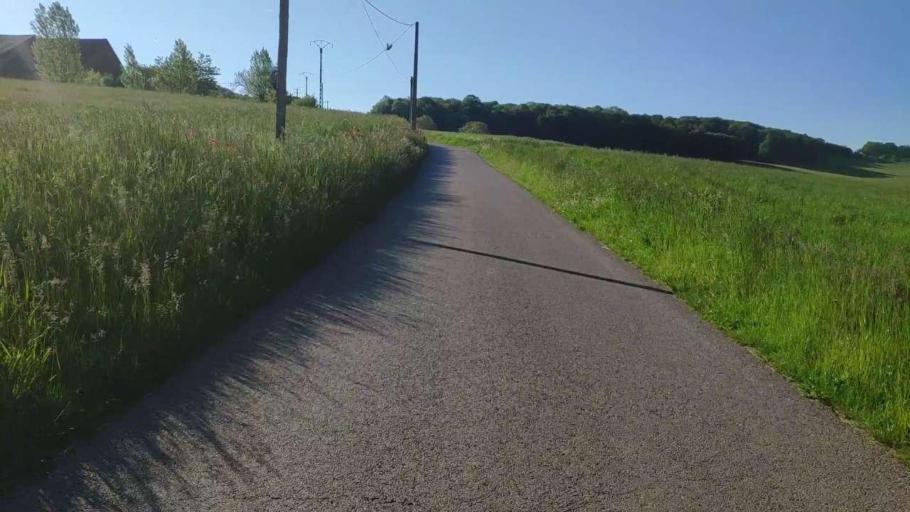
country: FR
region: Franche-Comte
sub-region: Departement du Jura
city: Perrigny
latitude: 46.7177
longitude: 5.6147
